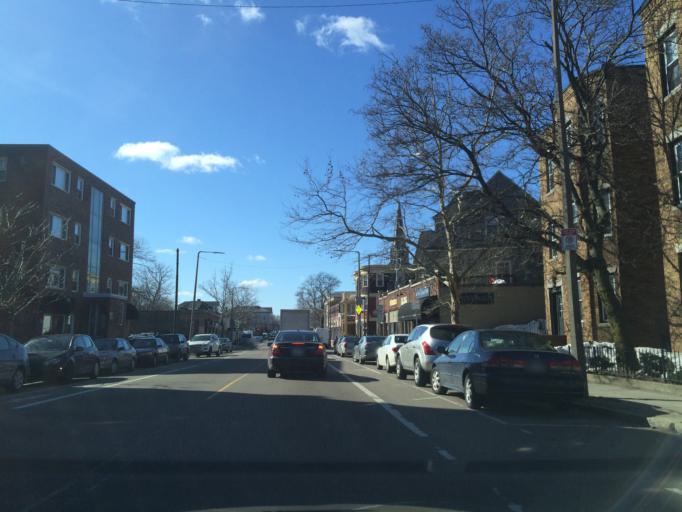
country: US
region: Massachusetts
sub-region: Suffolk County
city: Jamaica Plain
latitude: 42.3153
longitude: -71.1141
